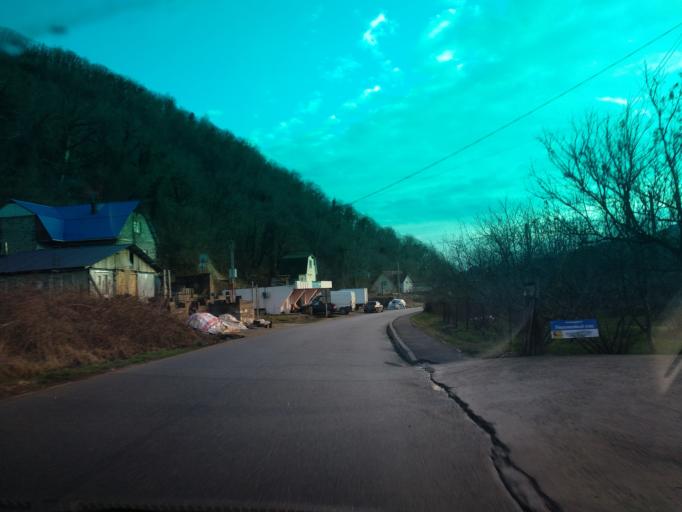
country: RU
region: Krasnodarskiy
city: Novomikhaylovskiy
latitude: 44.2681
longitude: 38.8295
